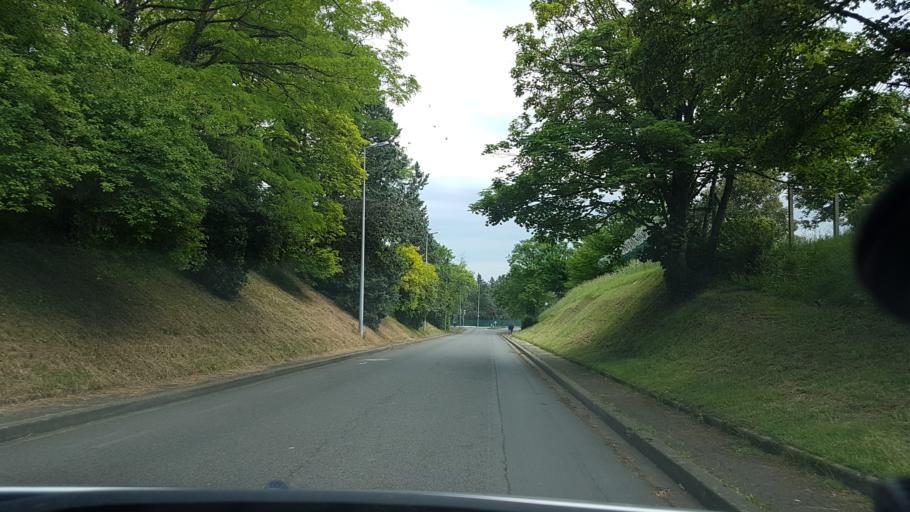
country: FR
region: Centre
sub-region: Departement du Cher
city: Bourges
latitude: 47.0957
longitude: 2.4001
